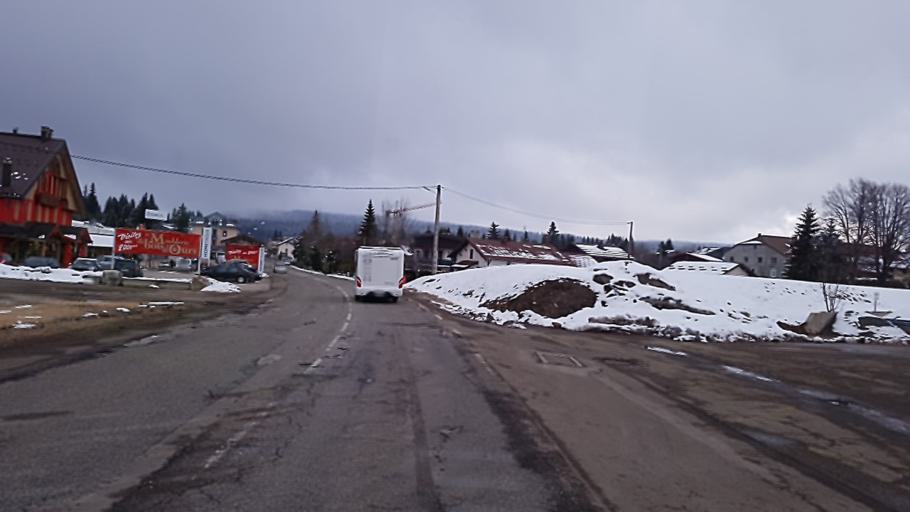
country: FR
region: Franche-Comte
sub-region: Departement du Jura
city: Les Rousses
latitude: 46.4778
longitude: 6.0648
